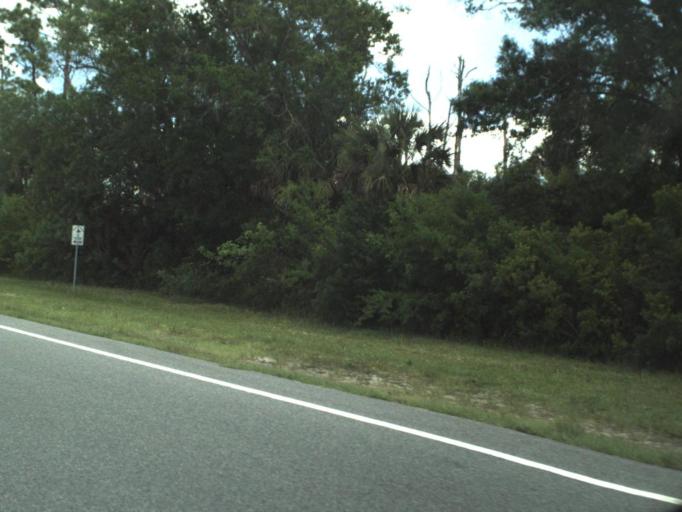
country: US
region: Florida
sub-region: Brevard County
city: Cocoa West
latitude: 28.3754
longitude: -80.8028
